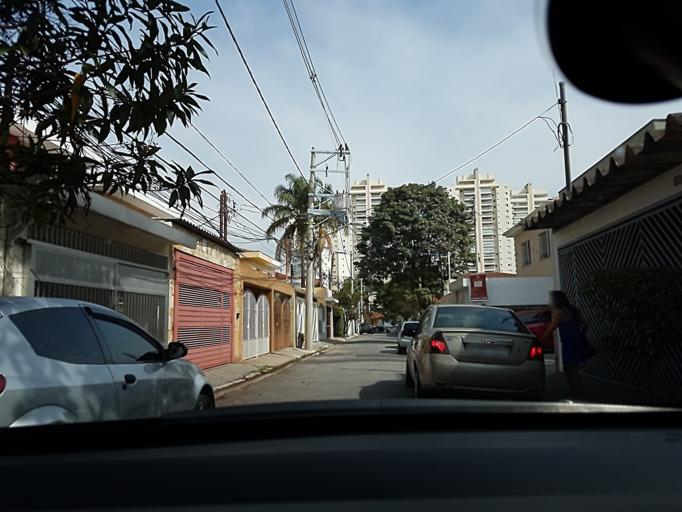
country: BR
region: Sao Paulo
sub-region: Taboao Da Serra
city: Taboao da Serra
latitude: -23.6387
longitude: -46.7121
